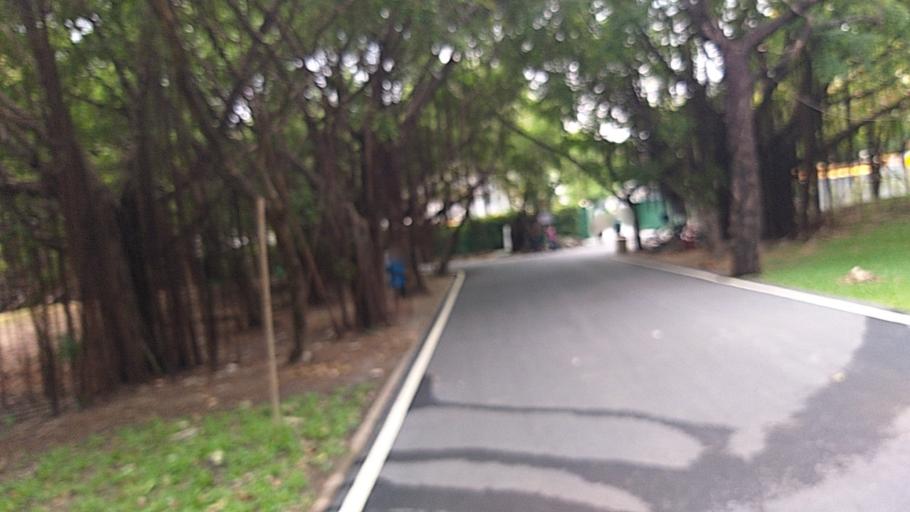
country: TH
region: Bangkok
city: Bang Sue
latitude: 13.8124
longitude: 100.5519
